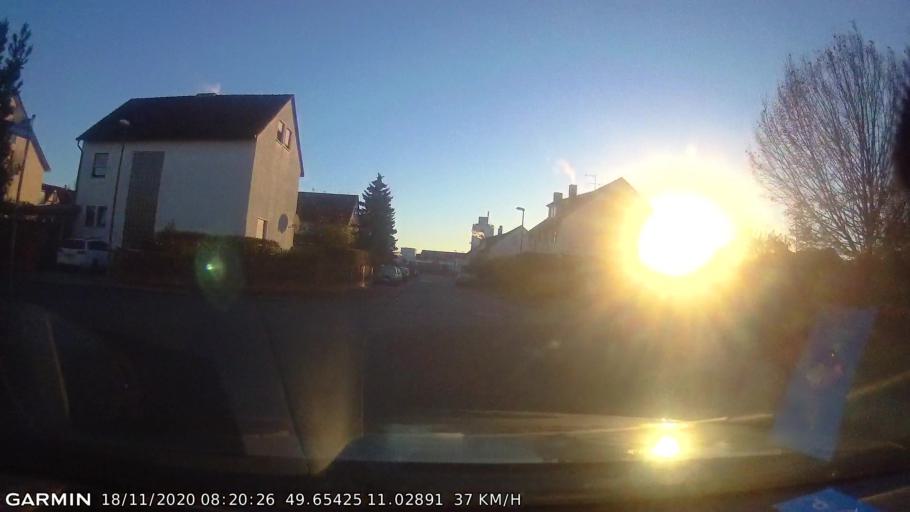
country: DE
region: Bavaria
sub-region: Regierungsbezirk Mittelfranken
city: Baiersdorf
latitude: 49.6544
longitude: 11.0292
